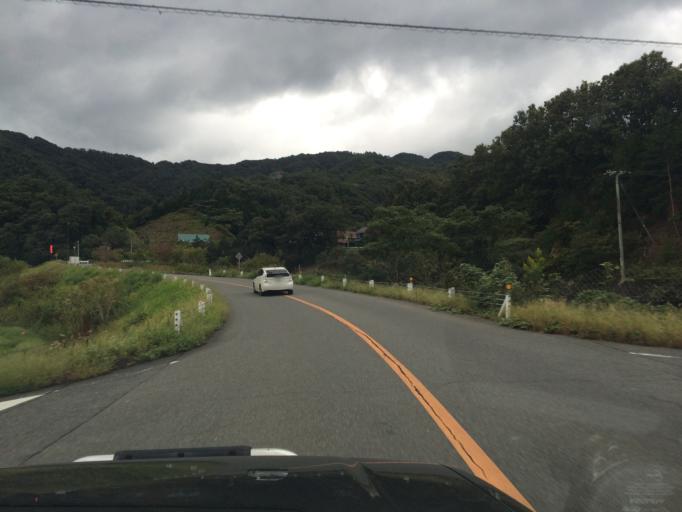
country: JP
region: Hyogo
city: Toyooka
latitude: 35.4376
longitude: 134.7949
